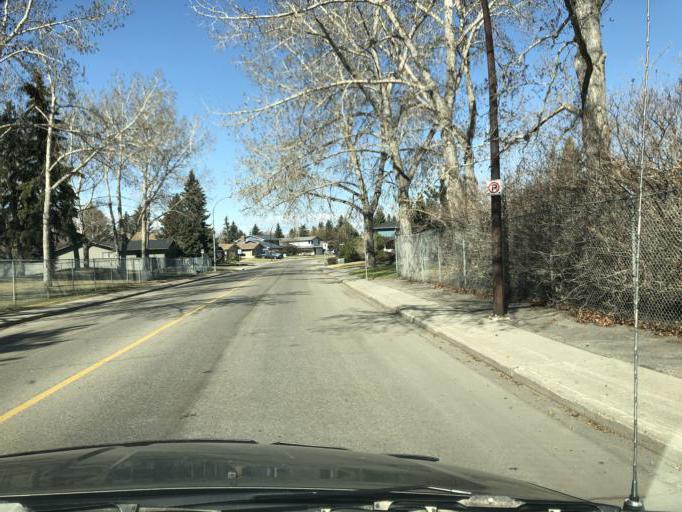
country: CA
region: Alberta
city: Calgary
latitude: 50.9373
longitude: -114.0516
